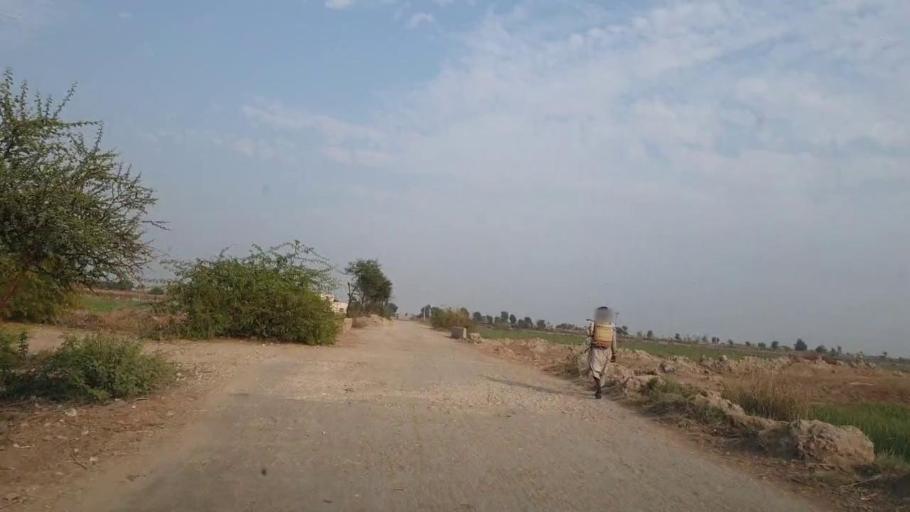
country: PK
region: Sindh
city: Pithoro
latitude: 25.5570
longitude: 69.2079
